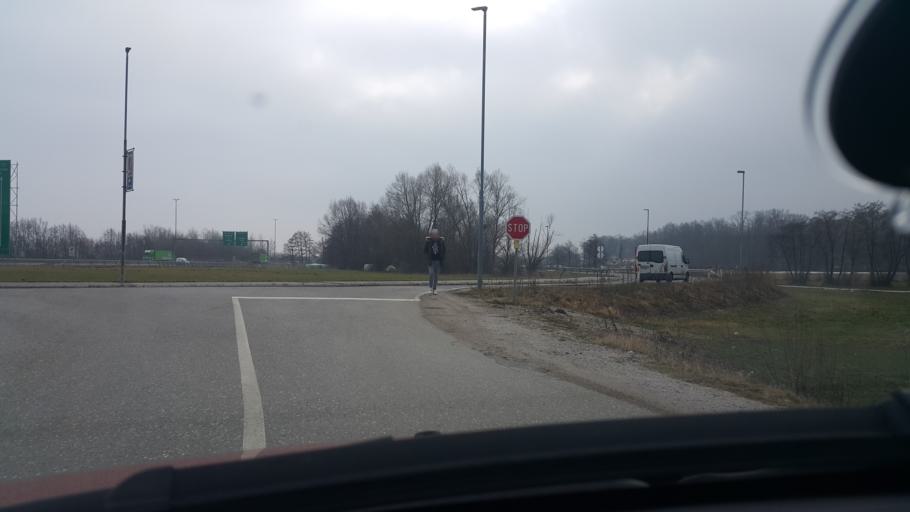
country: SI
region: Hoce-Slivnica
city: Spodnje Hoce
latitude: 46.4912
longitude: 15.6514
